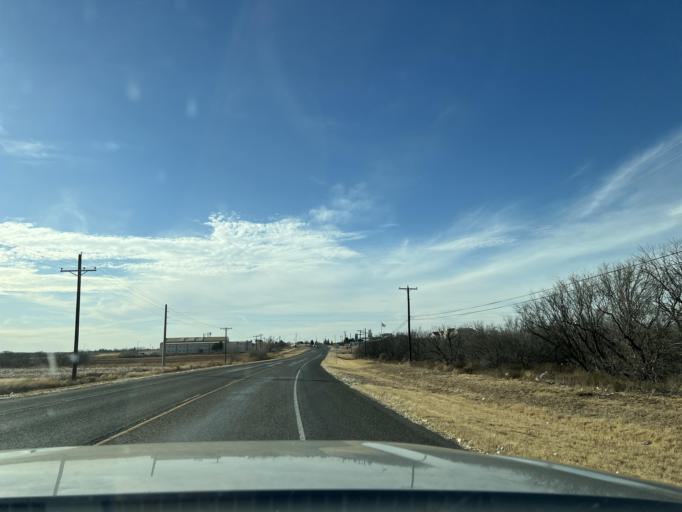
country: US
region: Texas
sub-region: Scurry County
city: Snyder
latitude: 32.7043
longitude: -100.8611
